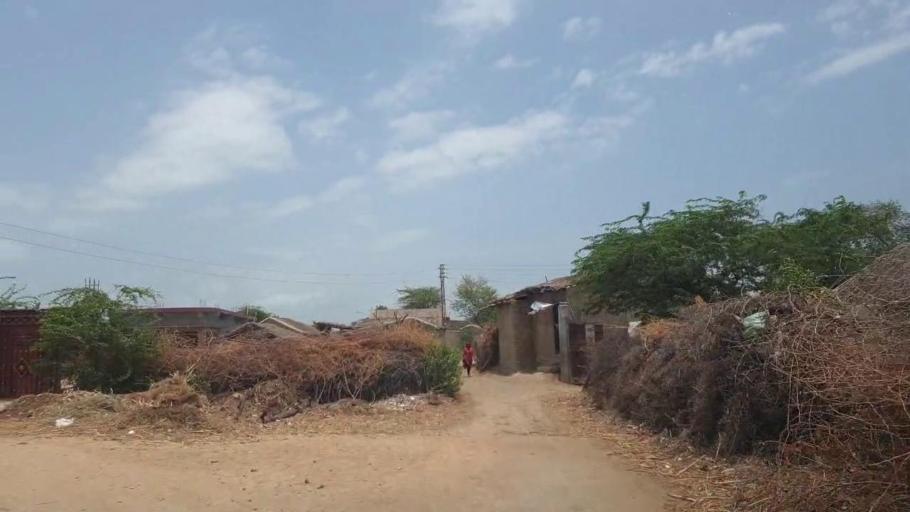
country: PK
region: Sindh
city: Badin
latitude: 24.6620
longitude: 68.9064
